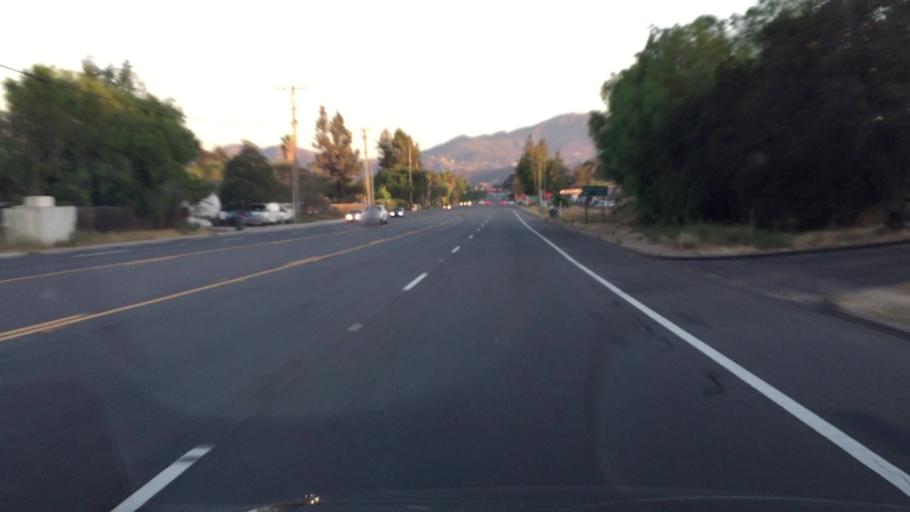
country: US
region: California
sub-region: San Diego County
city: Rancho San Diego
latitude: 32.7727
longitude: -116.9280
